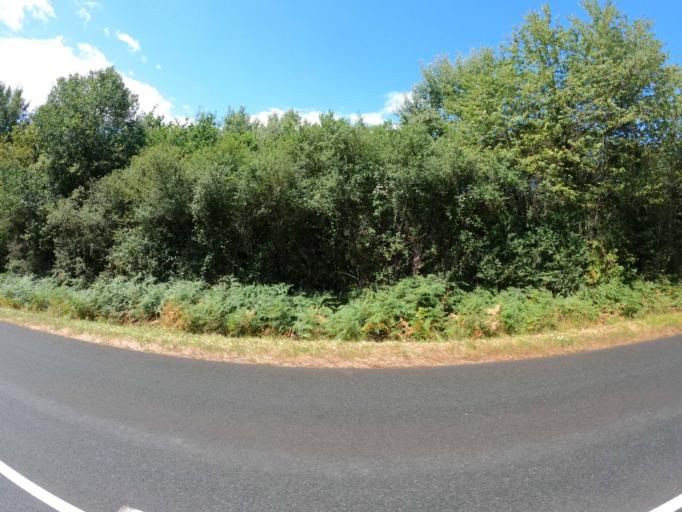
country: FR
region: Pays de la Loire
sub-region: Departement de Maine-et-Loire
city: Feneu
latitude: 47.6147
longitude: -0.5846
